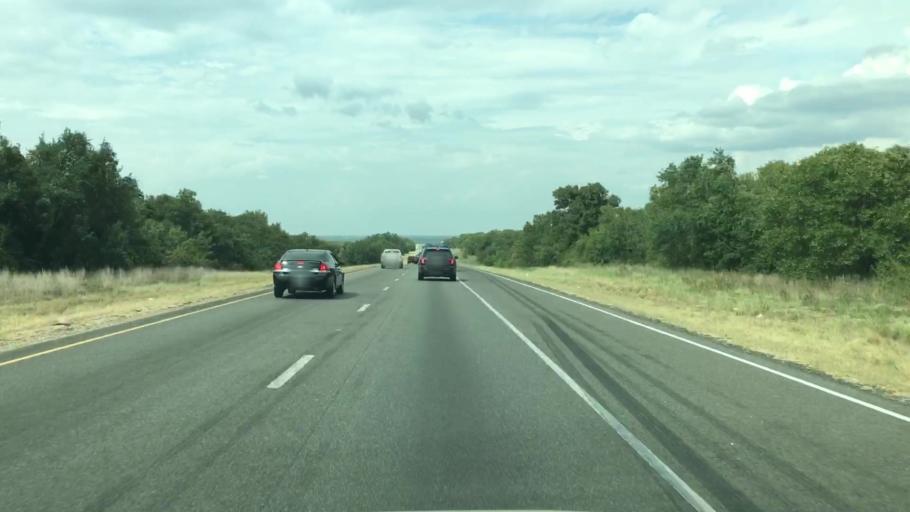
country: US
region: Texas
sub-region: Bexar County
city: Elmendorf
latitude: 29.1895
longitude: -98.4234
